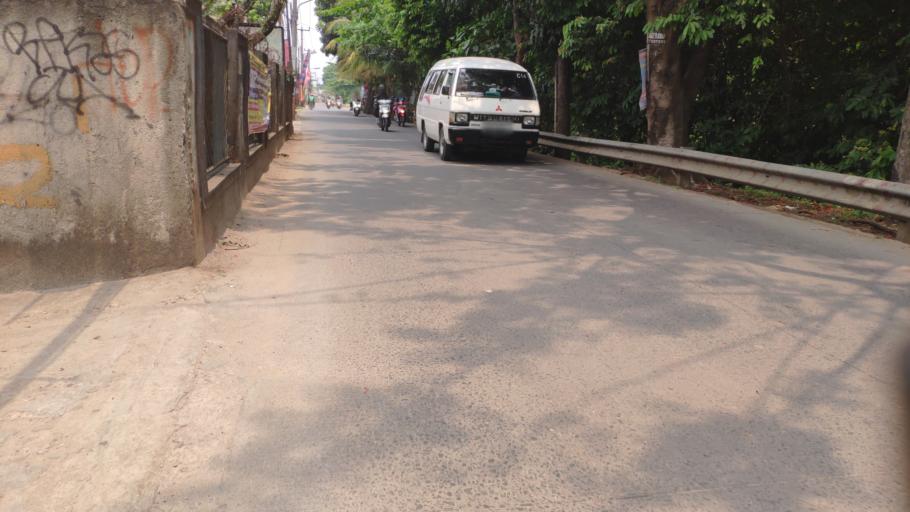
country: ID
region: West Java
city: Sawangan
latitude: -6.3788
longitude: 106.7901
